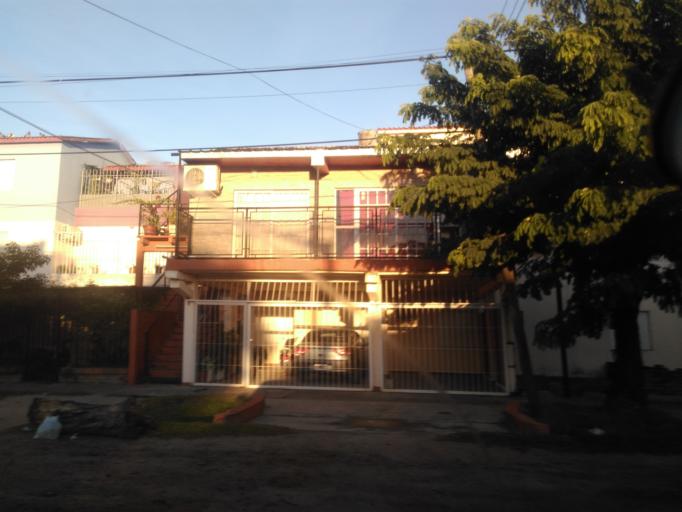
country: AR
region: Chaco
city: Resistencia
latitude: -27.4702
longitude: -58.9848
